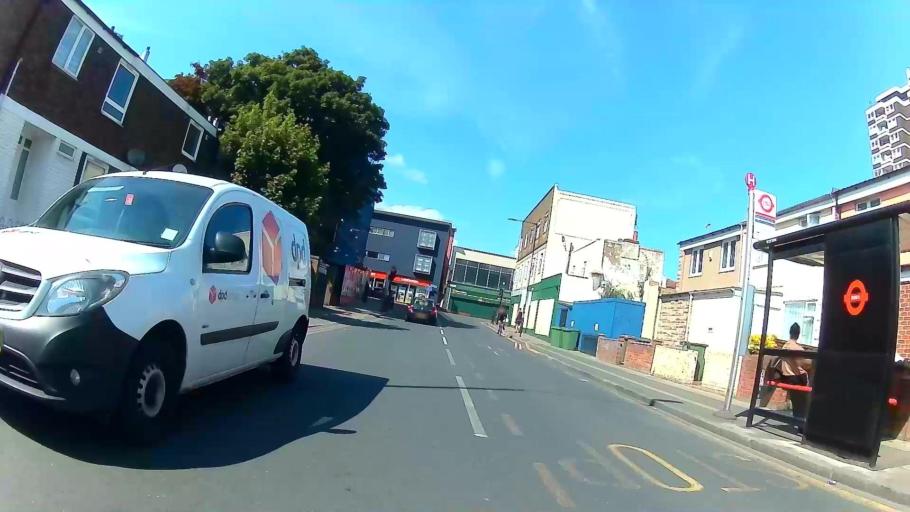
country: GB
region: England
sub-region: Greater London
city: East Ham
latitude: 51.5305
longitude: 0.0190
